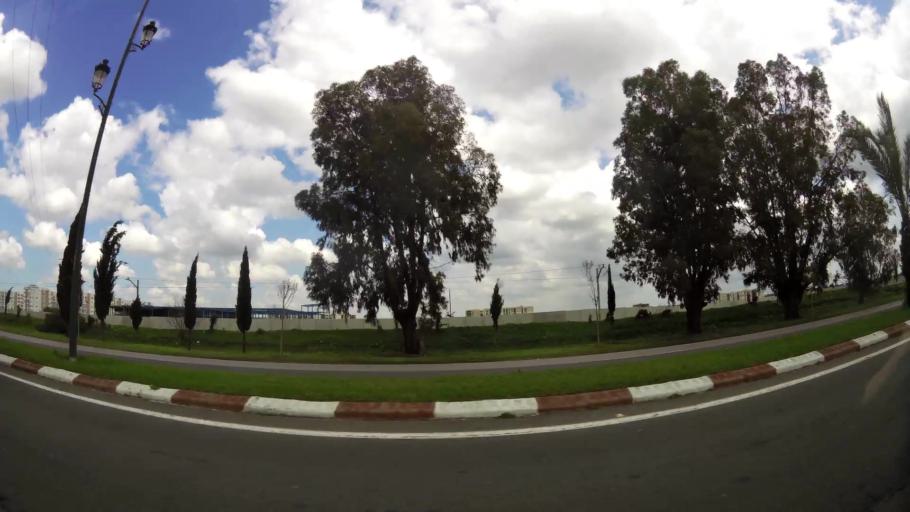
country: MA
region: Chaouia-Ouardigha
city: Nouaseur
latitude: 33.3877
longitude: -7.5656
